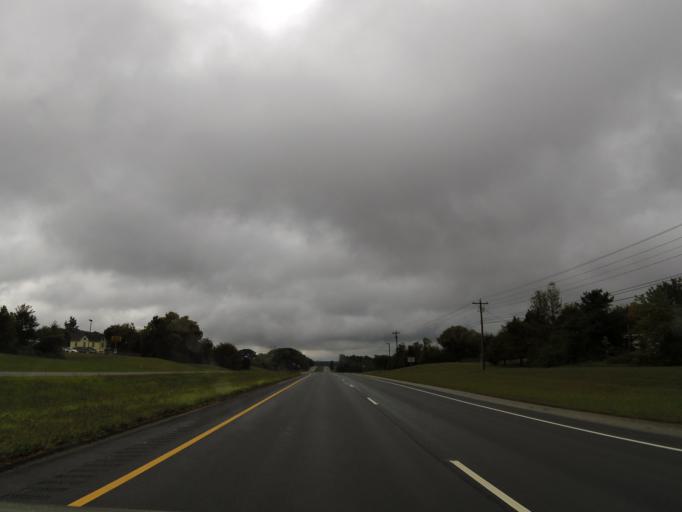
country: US
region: Tennessee
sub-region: Loudon County
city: Greenback
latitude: 35.7497
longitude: -84.1464
